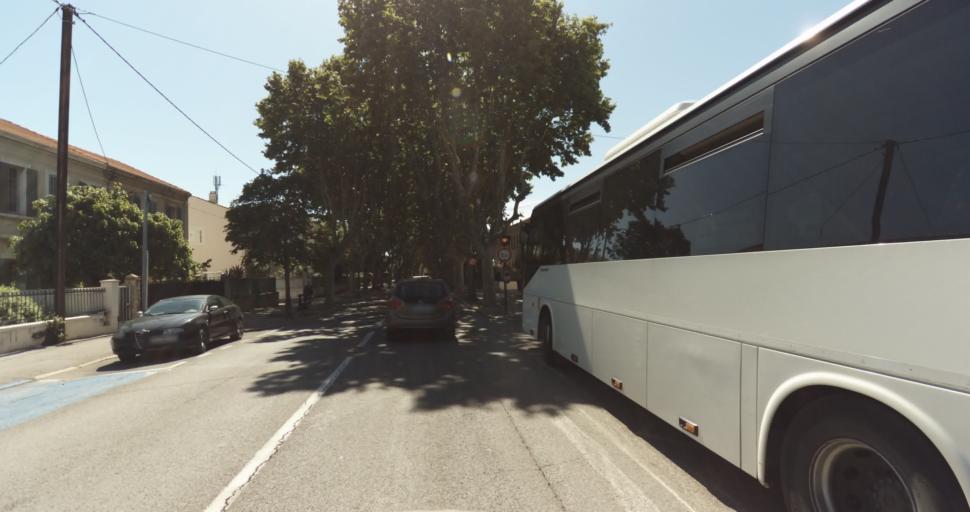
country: FR
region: Provence-Alpes-Cote d'Azur
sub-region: Departement du Var
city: La Seyne-sur-Mer
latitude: 43.1041
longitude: 5.8715
